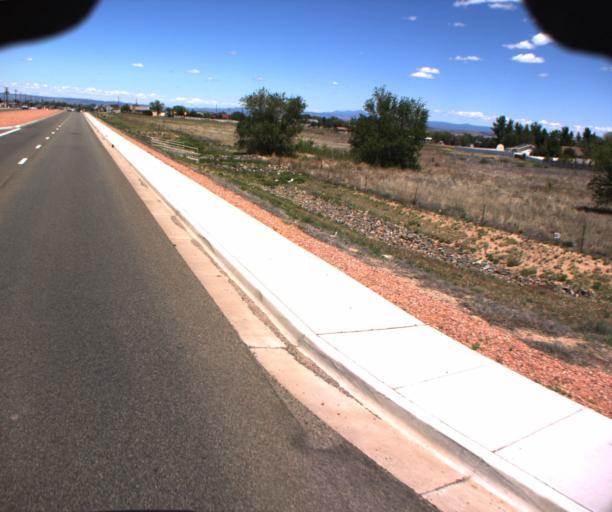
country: US
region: Arizona
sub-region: Yavapai County
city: Chino Valley
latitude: 34.7266
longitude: -112.4537
